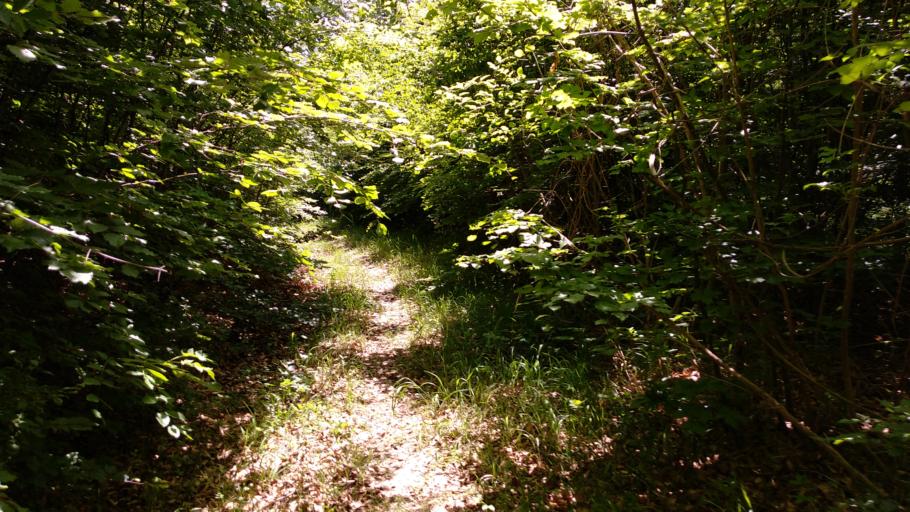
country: DE
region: North Rhine-Westphalia
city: Beverungen
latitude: 51.6423
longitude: 9.3640
